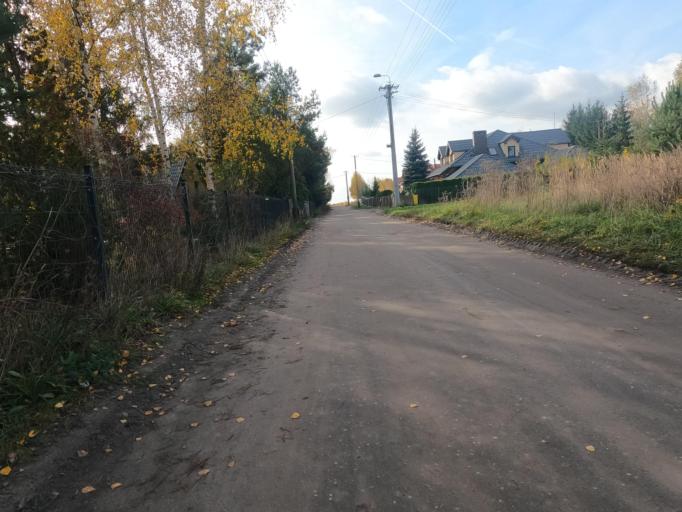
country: PL
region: Pomeranian Voivodeship
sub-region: Powiat starogardzki
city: Starogard Gdanski
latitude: 53.9789
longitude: 18.4860
